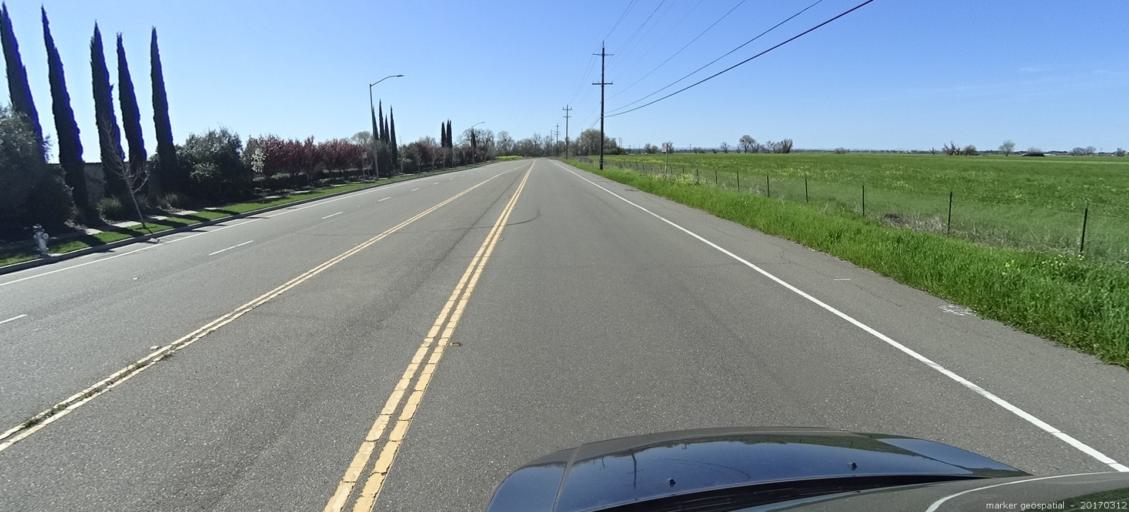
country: US
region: California
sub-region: Yolo County
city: West Sacramento
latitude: 38.6556
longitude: -121.5537
